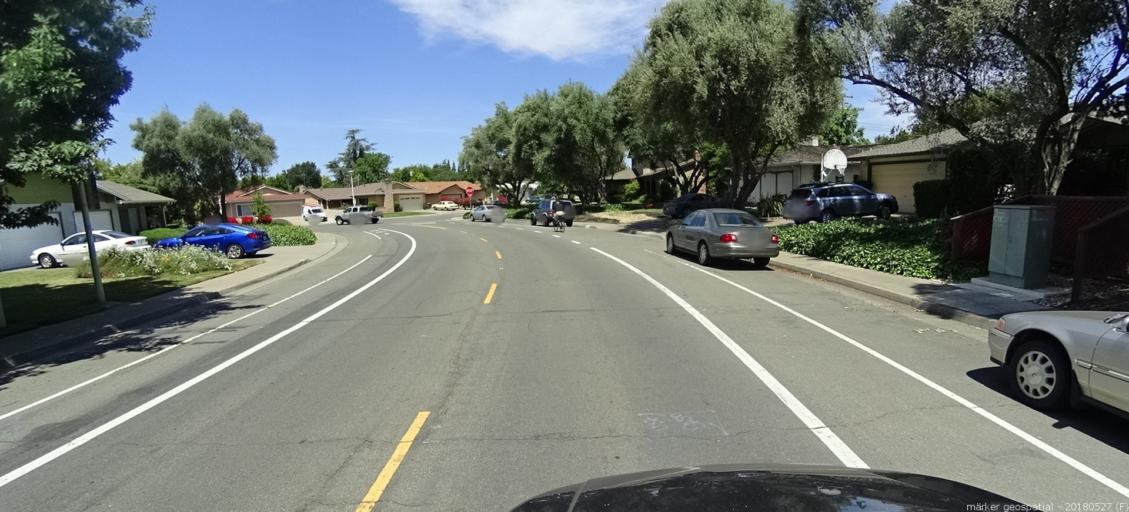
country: US
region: California
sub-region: Sacramento County
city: Rosemont
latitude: 38.5501
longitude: -121.3948
